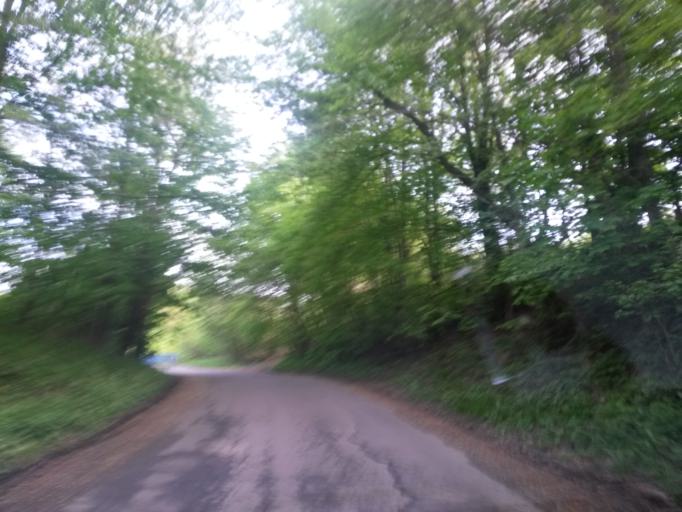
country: DE
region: North Rhine-Westphalia
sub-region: Regierungsbezirk Arnsberg
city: Schalksmuhle
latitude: 51.2927
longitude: 7.5545
